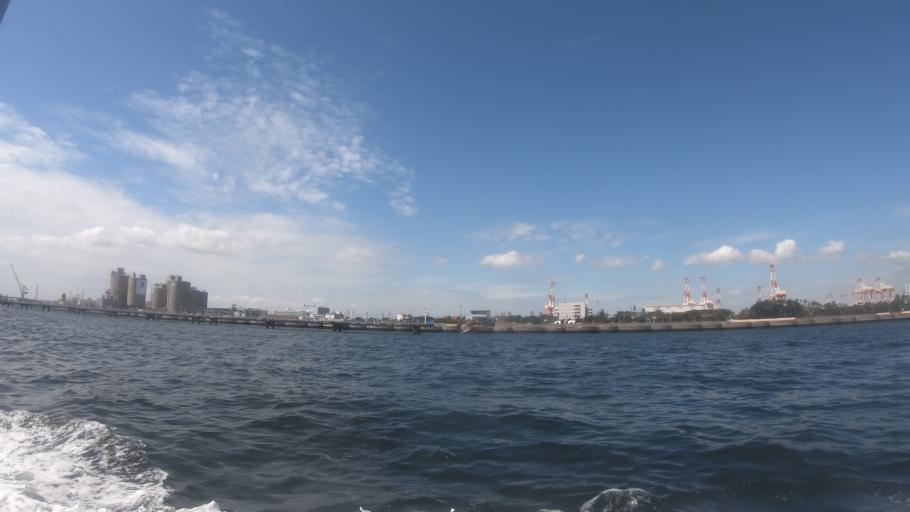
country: JP
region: Kanagawa
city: Yokohama
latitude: 35.4298
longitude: 139.6897
